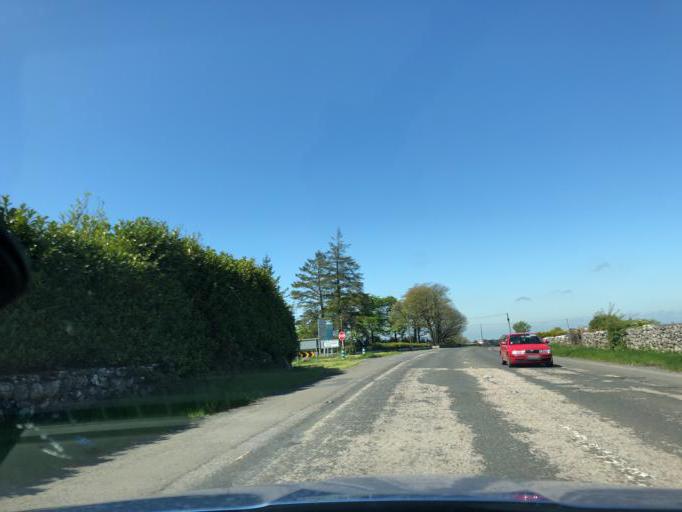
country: IE
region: Connaught
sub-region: County Galway
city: Athenry
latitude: 53.2143
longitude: -8.6994
